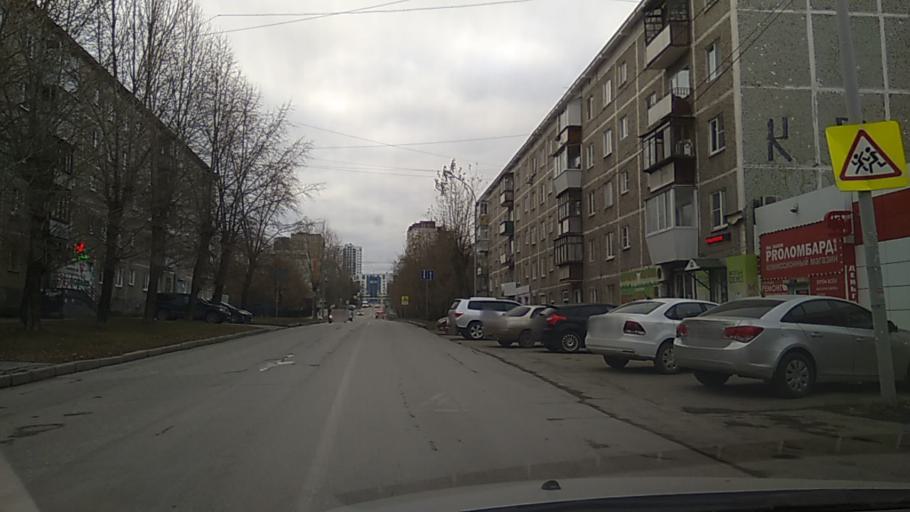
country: RU
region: Sverdlovsk
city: Yekaterinburg
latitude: 56.8303
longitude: 60.5517
